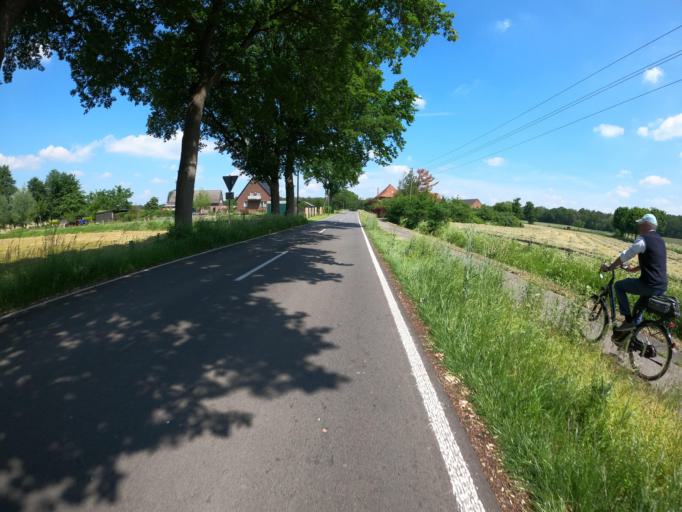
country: DE
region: North Rhine-Westphalia
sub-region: Regierungsbezirk Dusseldorf
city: Hunxe
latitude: 51.6789
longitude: 6.7862
